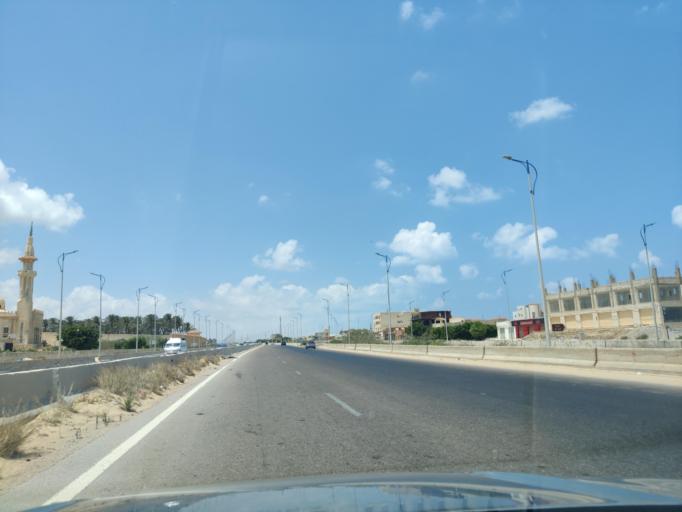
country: EG
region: Alexandria
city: Alexandria
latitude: 30.9869
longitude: 29.5881
